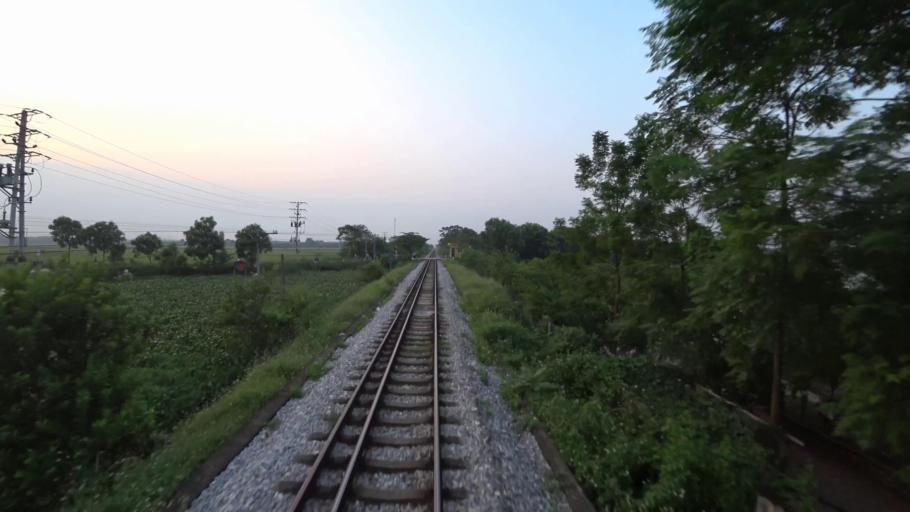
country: VN
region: Ha Noi
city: Dong Anh
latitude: 21.1242
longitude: 105.8824
